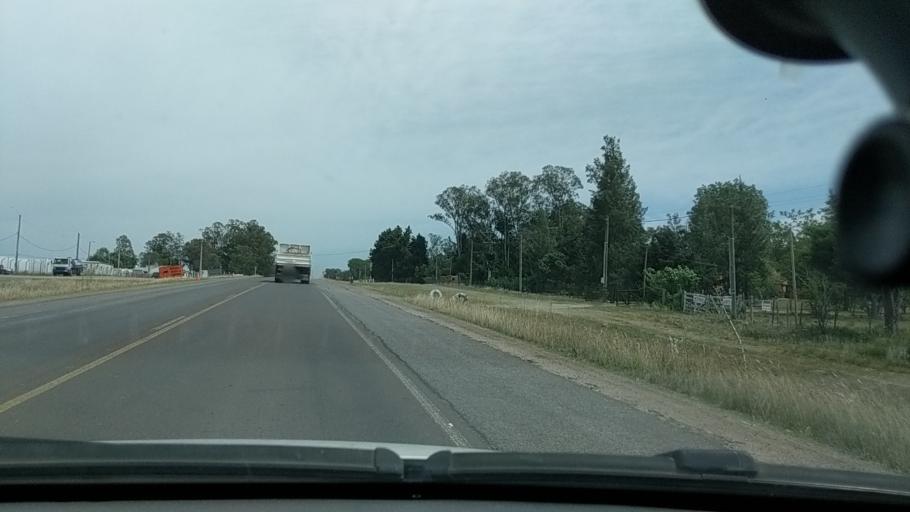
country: UY
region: Durazno
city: Durazno
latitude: -33.4197
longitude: -56.5044
